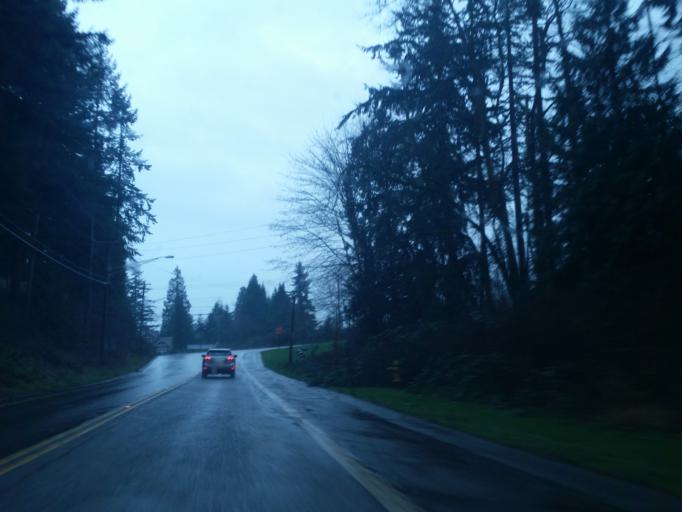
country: US
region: Washington
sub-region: Snohomish County
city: Meadowdale
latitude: 47.8724
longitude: -122.3087
